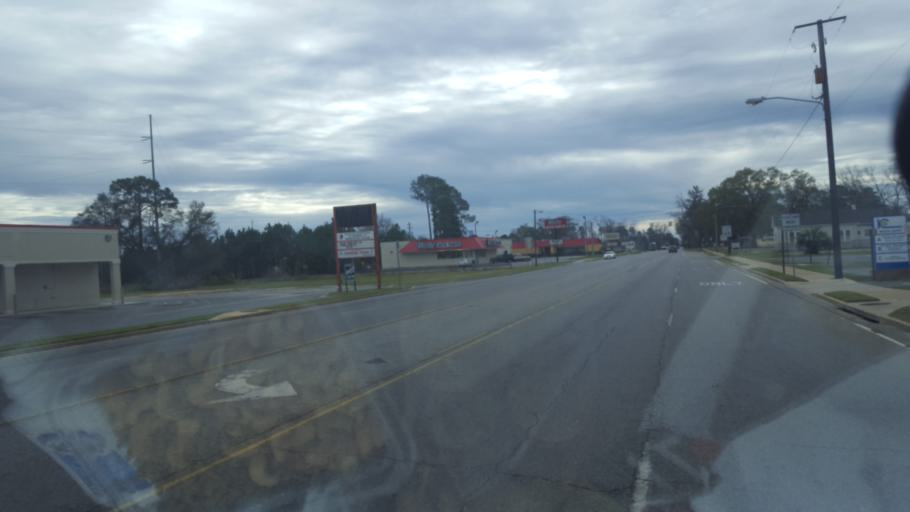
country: US
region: Georgia
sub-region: Irwin County
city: Ocilla
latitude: 31.6024
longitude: -83.2504
